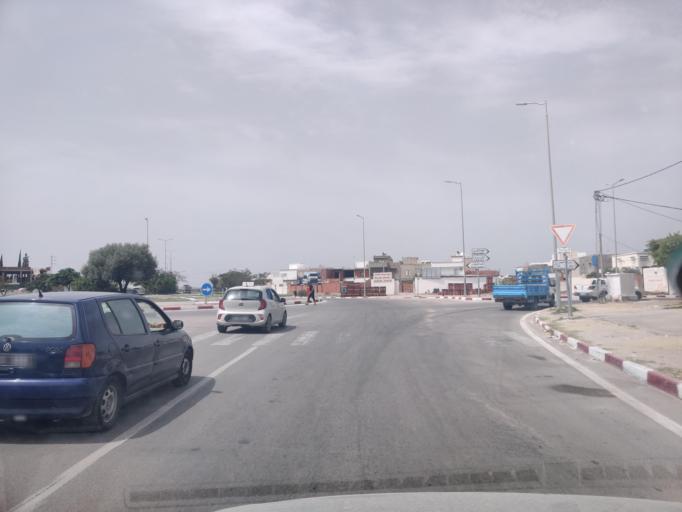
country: TN
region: Susah
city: Akouda
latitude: 35.8355
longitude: 10.5594
